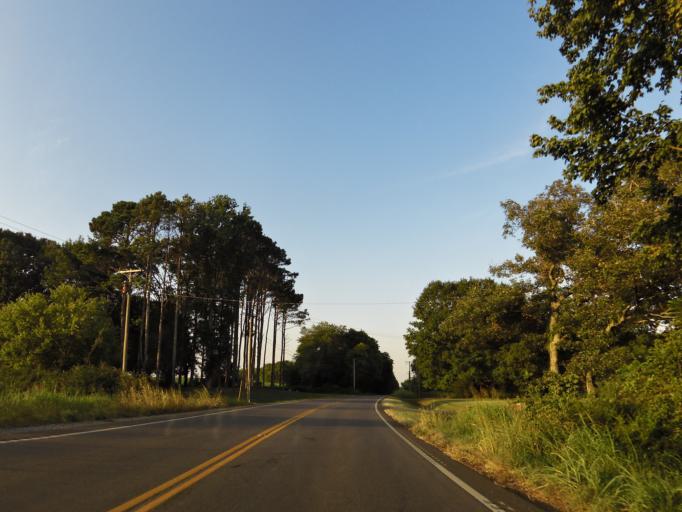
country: US
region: Tennessee
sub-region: Monroe County
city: Sweetwater
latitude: 35.5717
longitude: -84.4976
